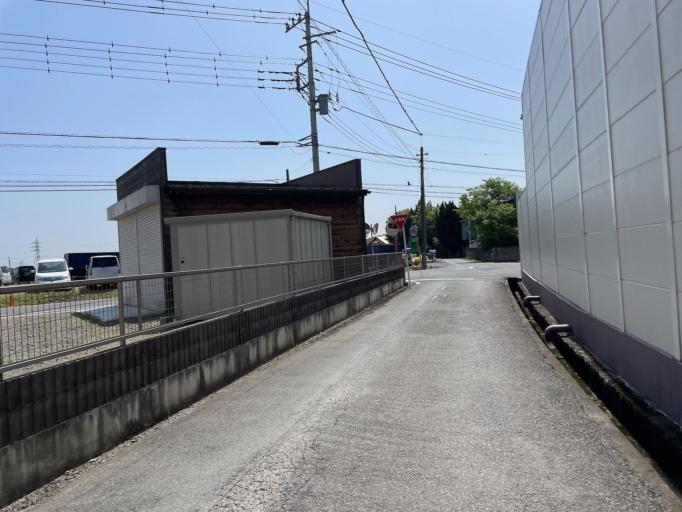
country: JP
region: Tochigi
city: Ashikaga
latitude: 36.3046
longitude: 139.4224
